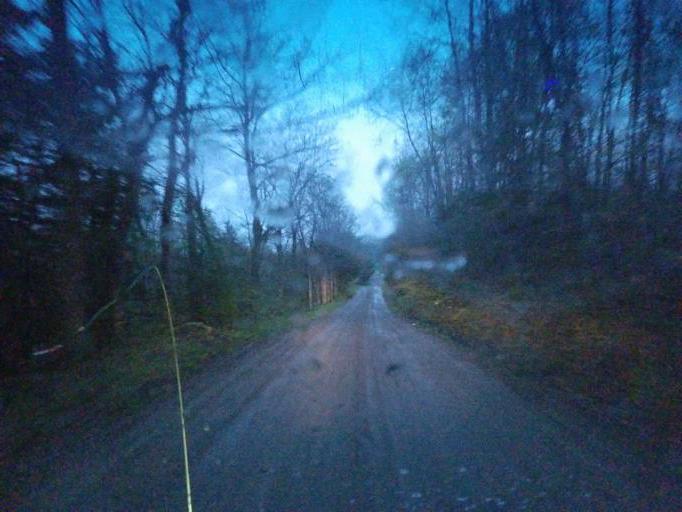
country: US
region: Pennsylvania
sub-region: Tioga County
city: Westfield
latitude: 41.9390
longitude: -77.7356
